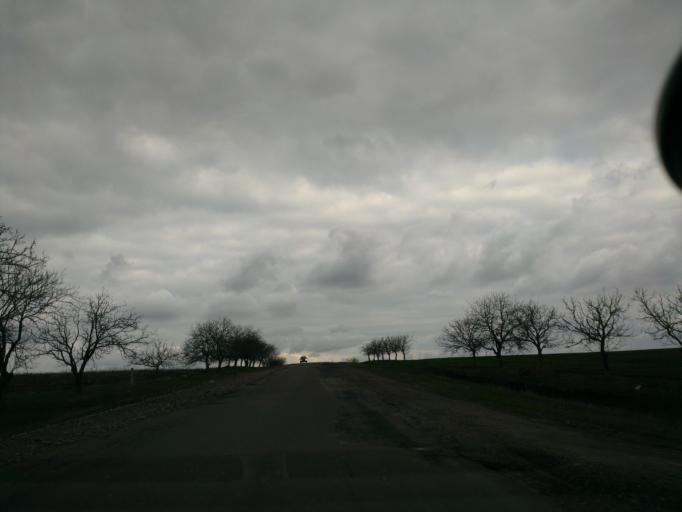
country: MD
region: Gagauzia
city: Comrat
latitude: 46.3086
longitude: 28.6053
